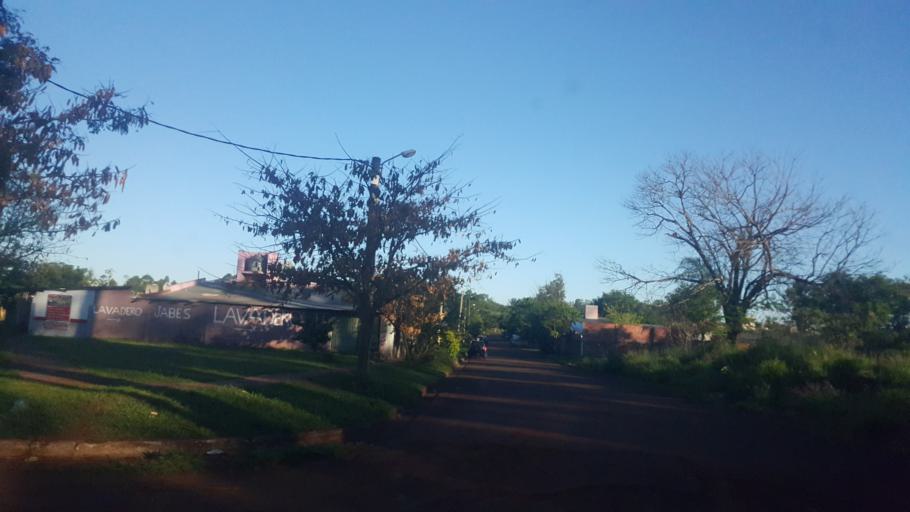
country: AR
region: Misiones
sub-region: Departamento de Capital
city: Posadas
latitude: -27.4248
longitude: -55.9443
